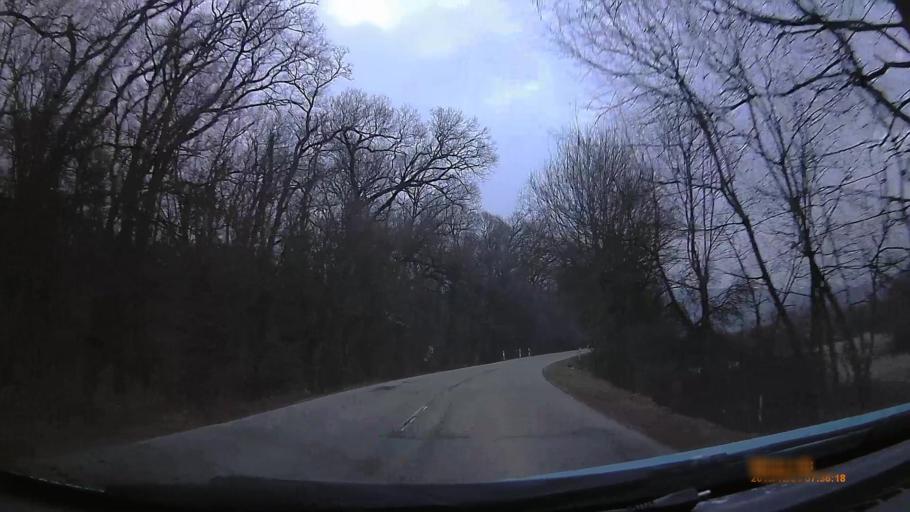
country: HU
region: Heves
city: Sirok
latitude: 47.9234
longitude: 20.1688
